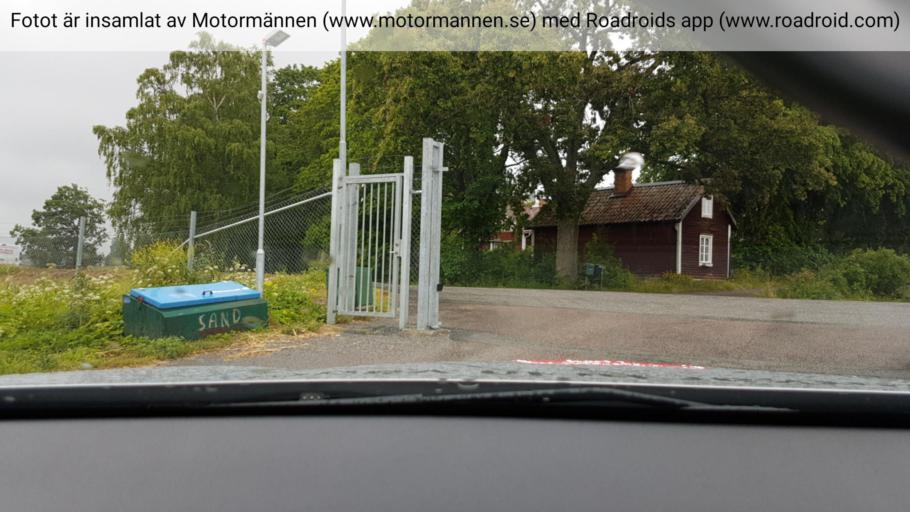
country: SE
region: Uppsala
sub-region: Knivsta Kommun
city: Knivsta
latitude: 59.7217
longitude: 17.7779
